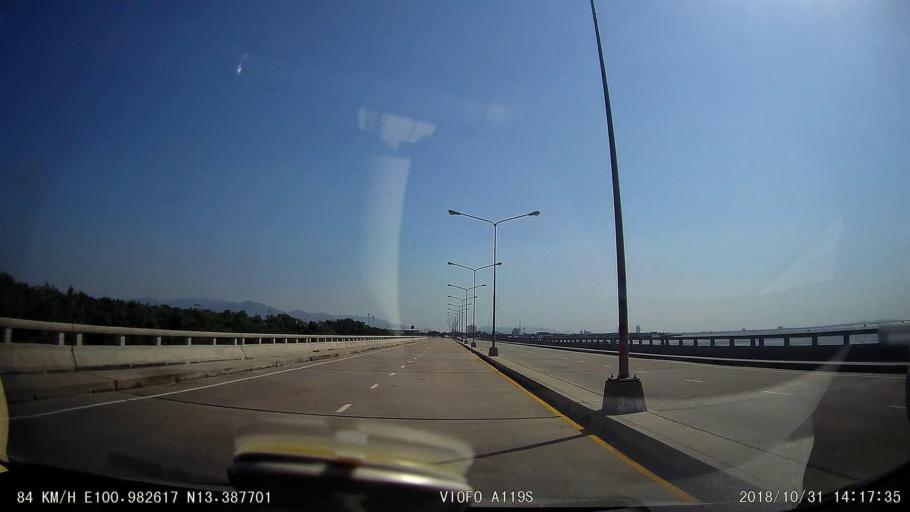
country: TH
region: Chon Buri
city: Chon Buri
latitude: 13.3878
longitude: 100.9827
